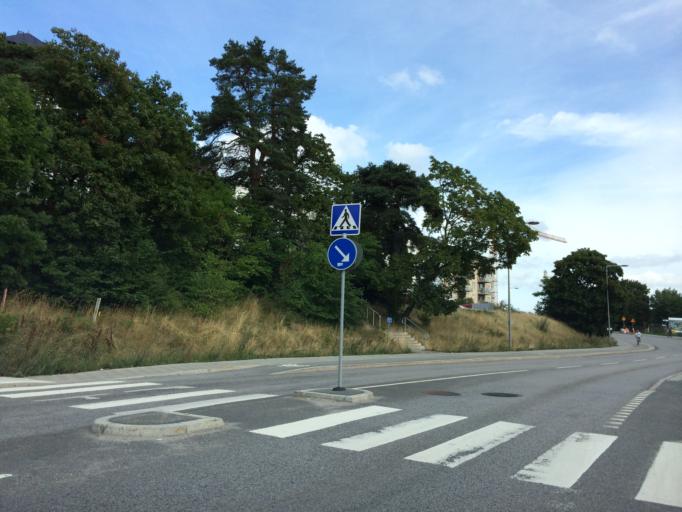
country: SE
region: Stockholm
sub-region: Stockholms Kommun
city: Arsta
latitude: 59.3019
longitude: 18.0271
